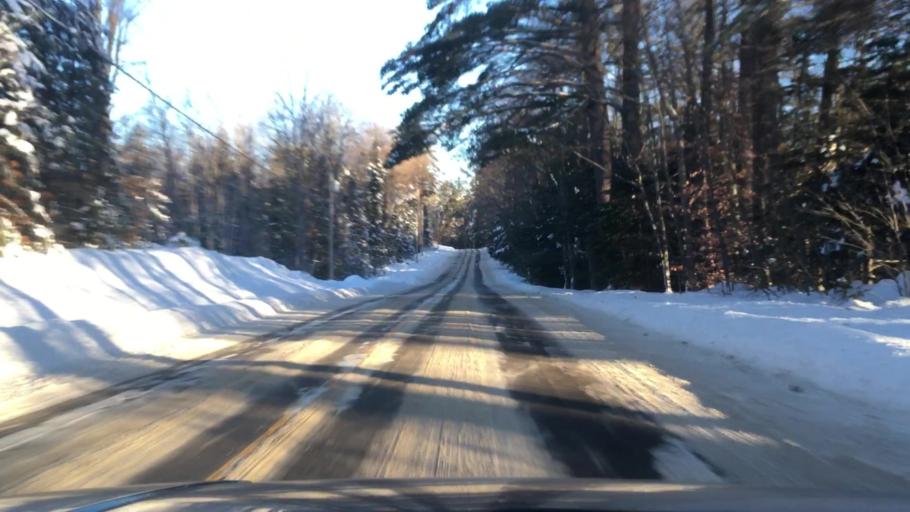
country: US
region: Maine
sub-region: Oxford County
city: Lovell
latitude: 44.1359
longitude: -70.9786
